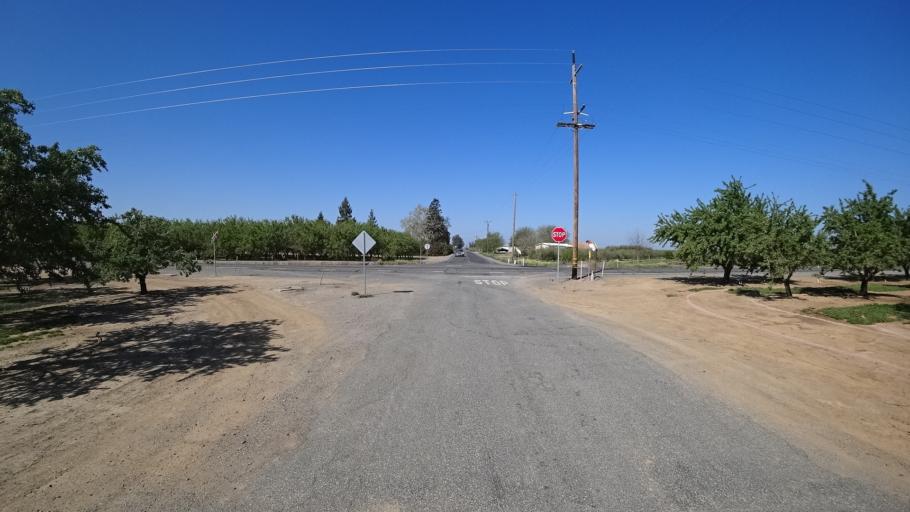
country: US
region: California
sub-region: Glenn County
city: Hamilton City
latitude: 39.6596
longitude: -122.0079
